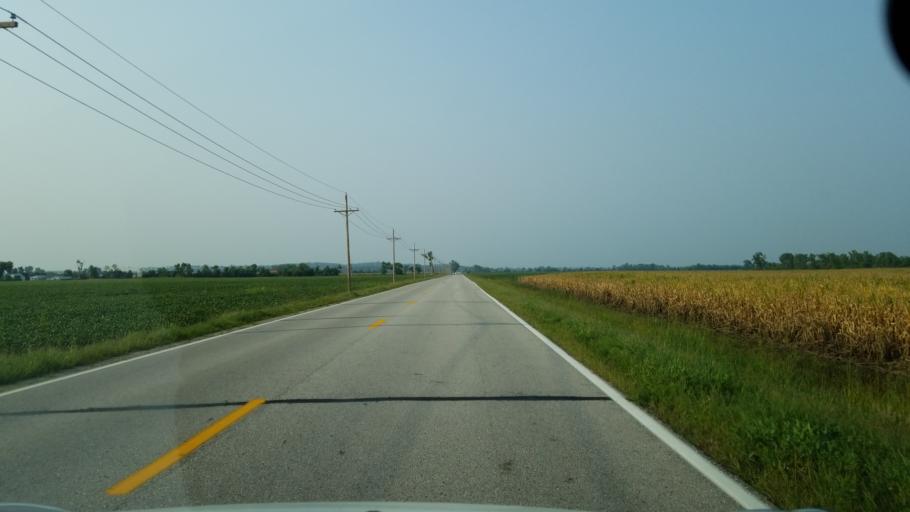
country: US
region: Nebraska
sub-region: Sarpy County
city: Offutt Air Force Base
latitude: 41.0913
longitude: -95.8898
